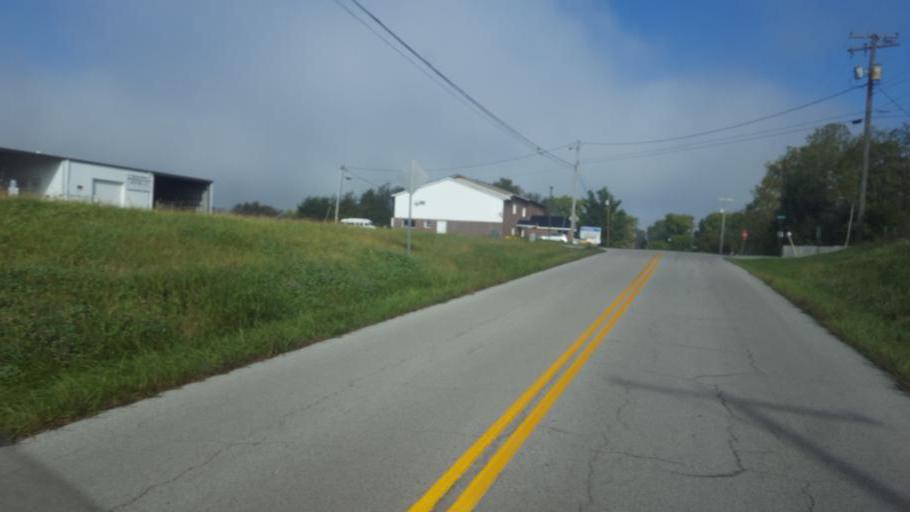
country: US
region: Kentucky
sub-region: Mason County
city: Maysville
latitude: 38.5589
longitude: -83.7737
